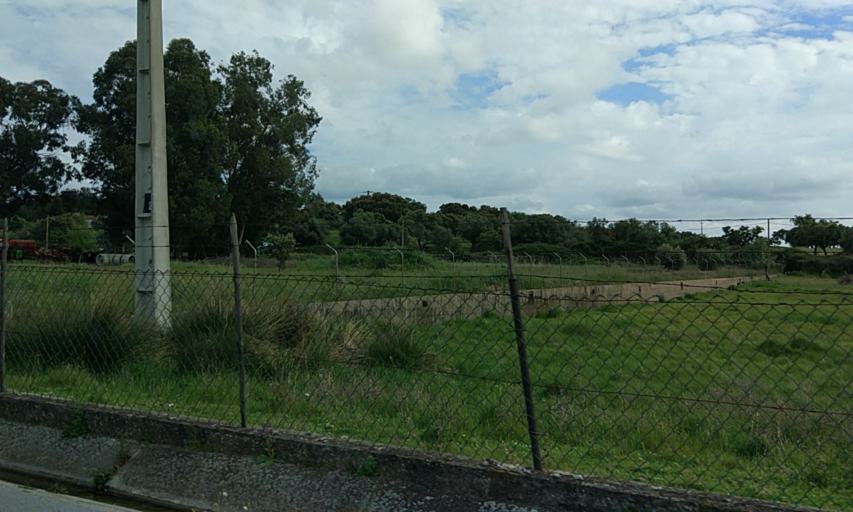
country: PT
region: Evora
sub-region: Evora
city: Evora
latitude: 38.5676
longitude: -7.9423
